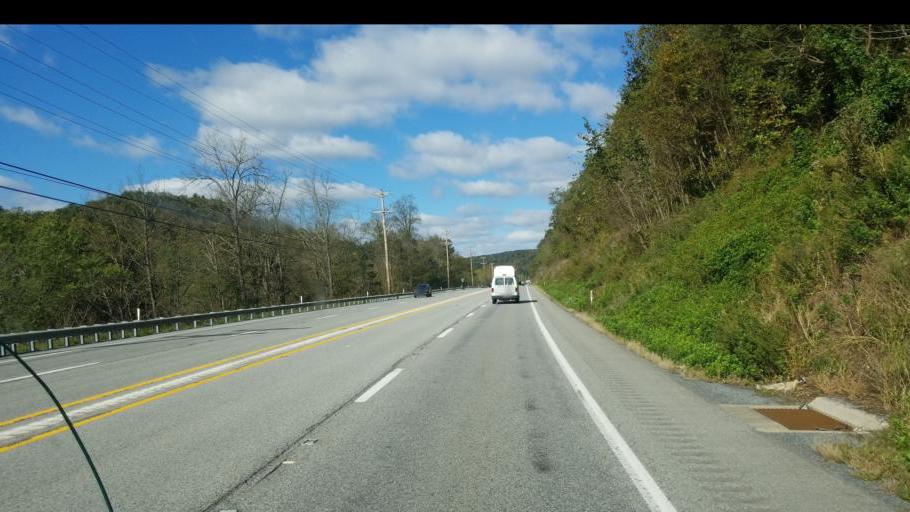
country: US
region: Pennsylvania
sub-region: Bedford County
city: Earlston
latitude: 39.9988
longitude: -78.2920
